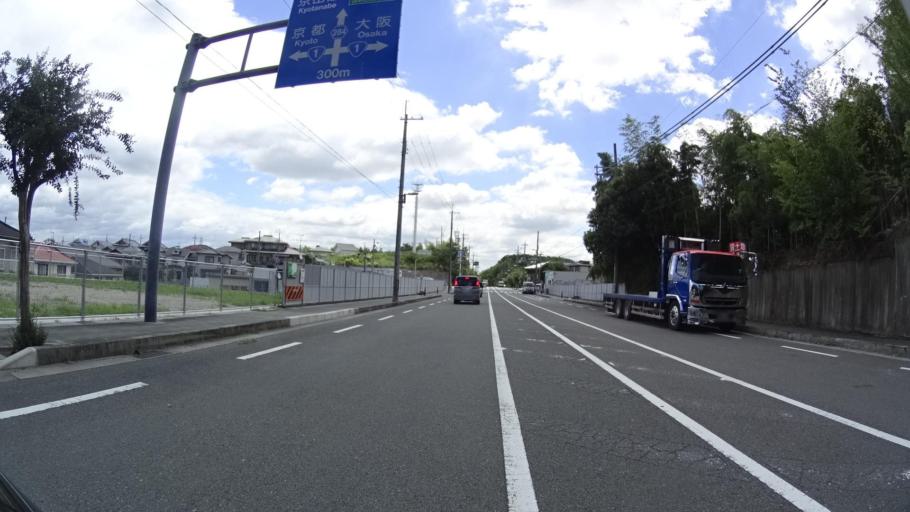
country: JP
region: Kyoto
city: Yawata
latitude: 34.8543
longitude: 135.7014
